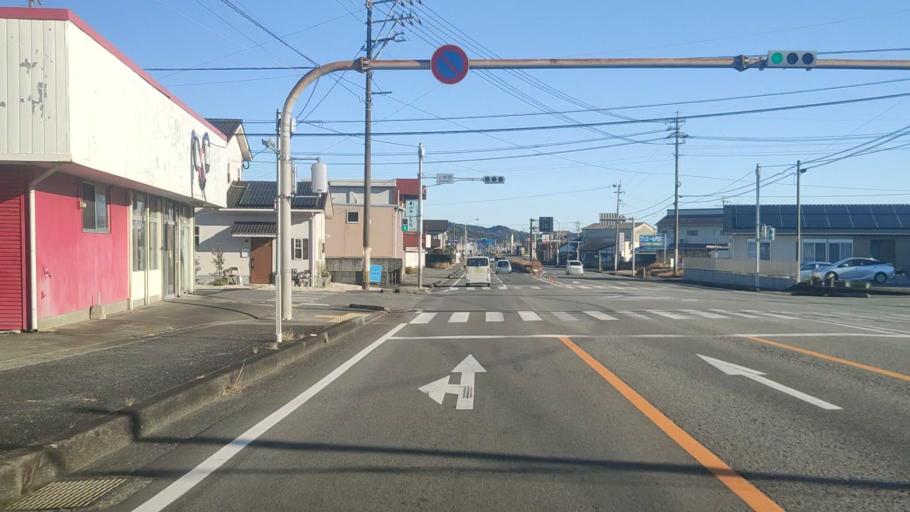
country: JP
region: Miyazaki
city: Nobeoka
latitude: 32.4743
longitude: 131.6527
